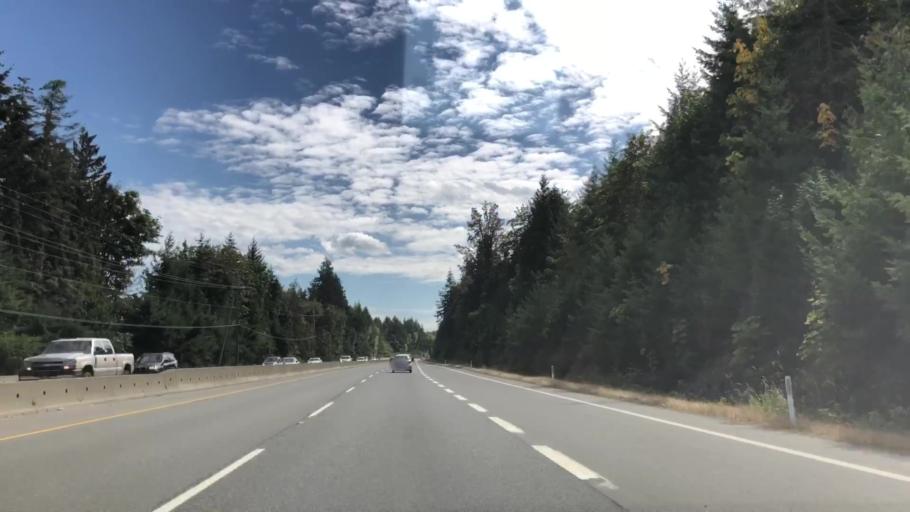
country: CA
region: British Columbia
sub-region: Cowichan Valley Regional District
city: Ladysmith
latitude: 48.9312
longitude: -123.7560
